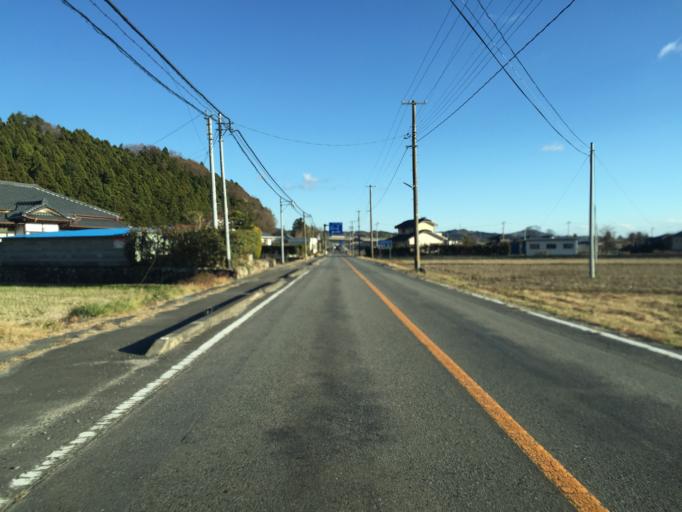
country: JP
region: Fukushima
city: Iwaki
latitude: 37.1378
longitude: 140.8499
